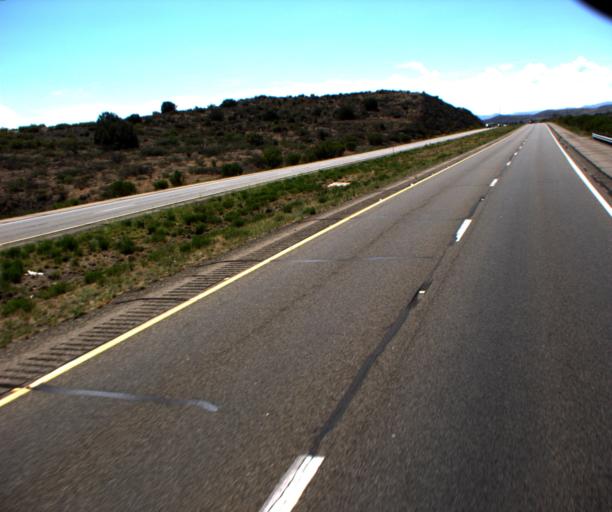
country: US
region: Arizona
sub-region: Yavapai County
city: Spring Valley
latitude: 34.3681
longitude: -112.1798
